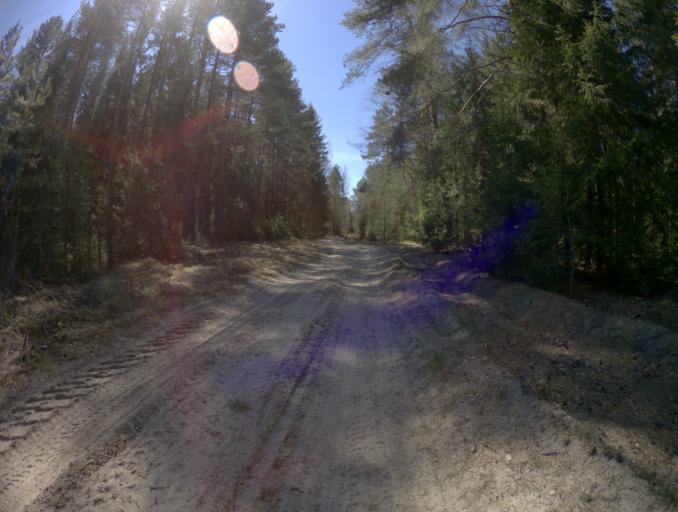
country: RU
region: Vladimir
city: Golovino
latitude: 55.9038
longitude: 40.4399
